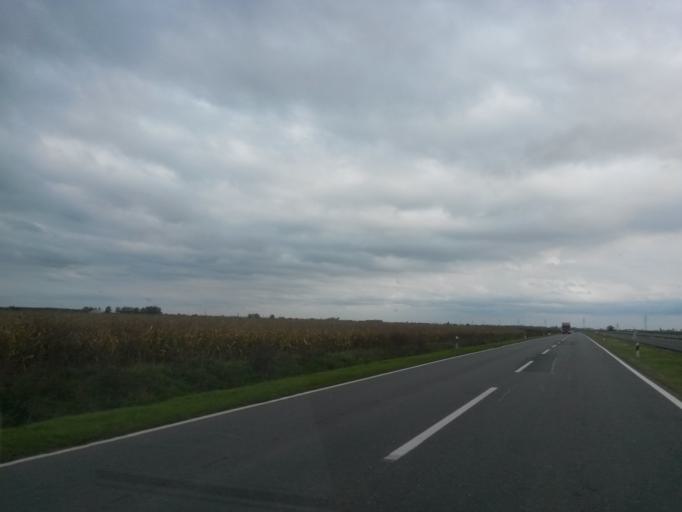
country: HR
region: Osjecko-Baranjska
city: Visnjevac
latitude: 45.5629
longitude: 18.5955
